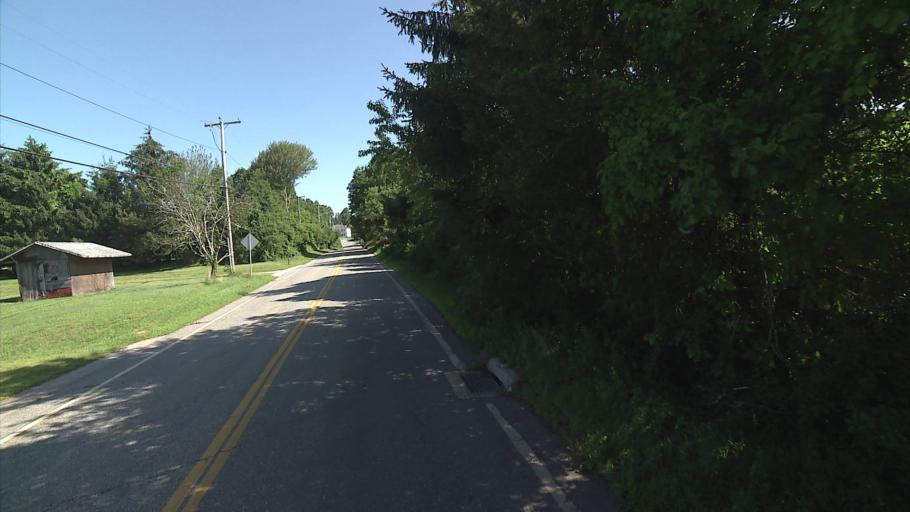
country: US
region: Connecticut
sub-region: New London County
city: Montville Center
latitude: 41.4806
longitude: -72.1612
